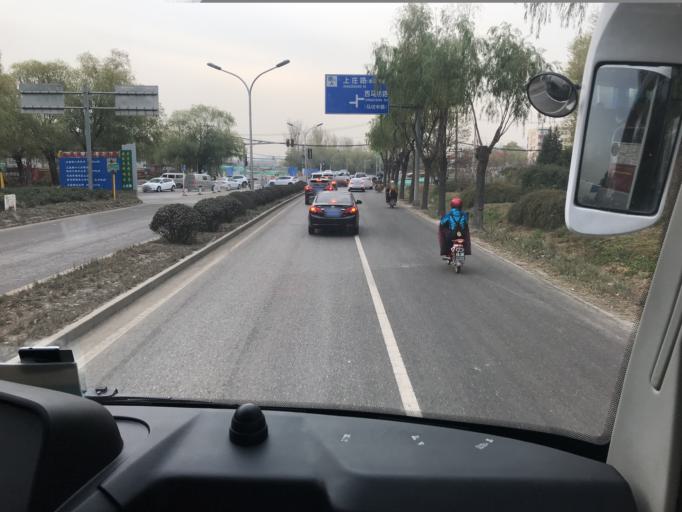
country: CN
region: Beijing
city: Sujiatuo
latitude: 40.0925
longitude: 116.2092
